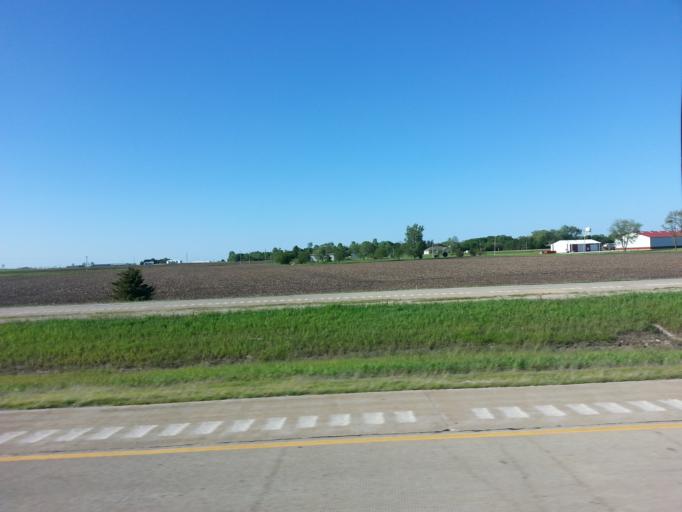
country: US
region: Illinois
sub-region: Woodford County
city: Minonk
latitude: 40.8931
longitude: -89.0500
